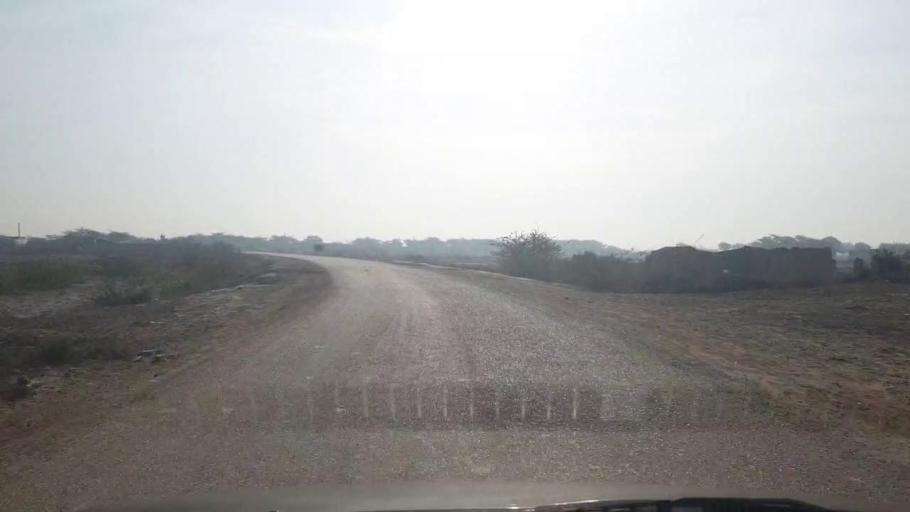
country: PK
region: Sindh
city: Umarkot
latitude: 25.3446
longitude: 69.7003
